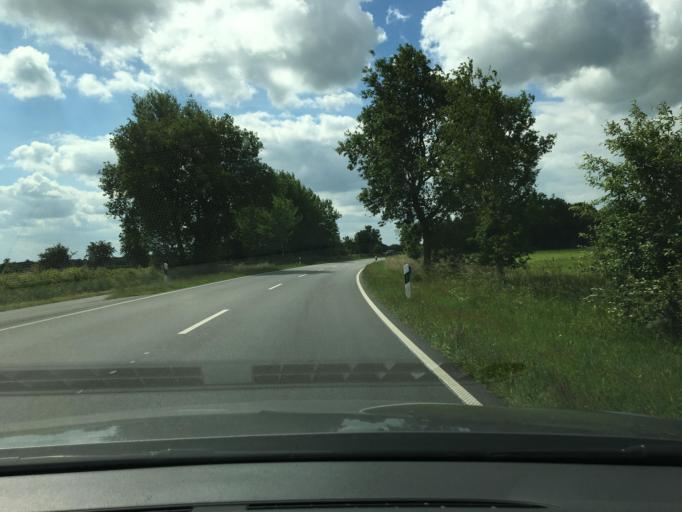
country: DE
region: Schleswig-Holstein
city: Kropp
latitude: 54.4243
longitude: 9.4942
